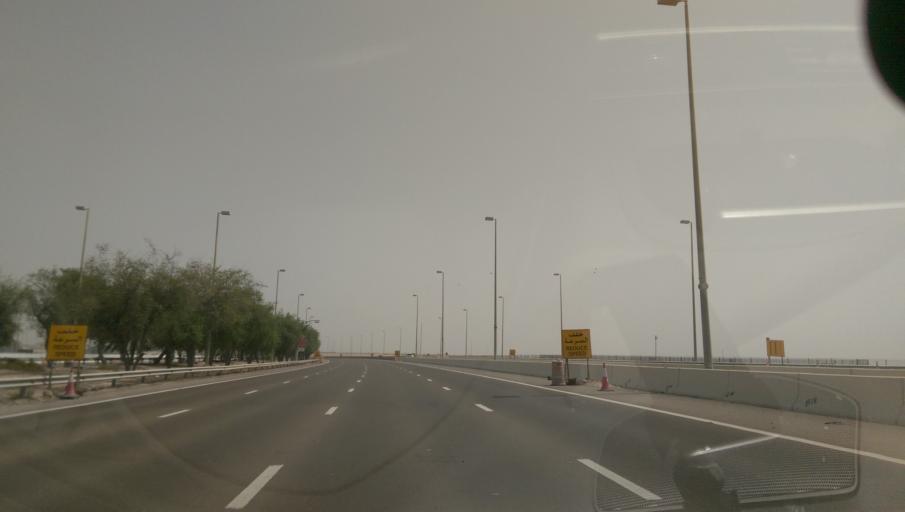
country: AE
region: Abu Dhabi
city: Abu Dhabi
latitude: 24.4162
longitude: 54.6763
